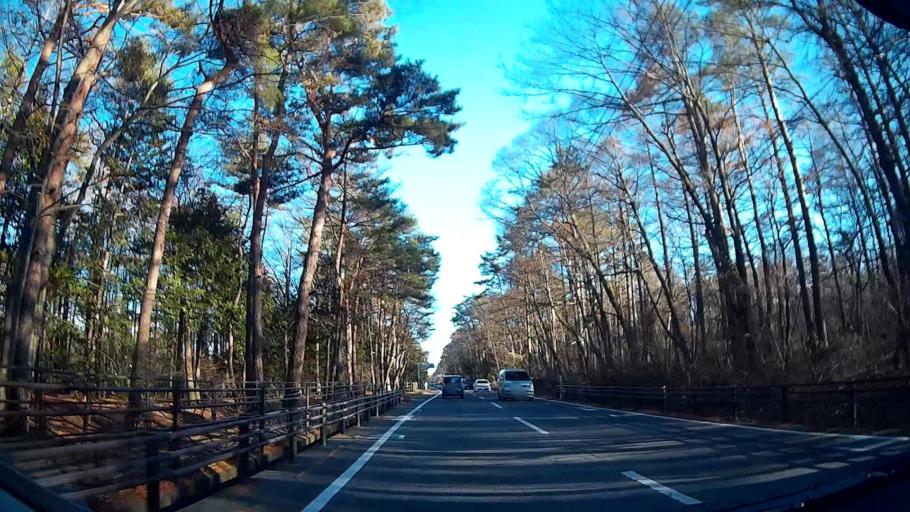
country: JP
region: Yamanashi
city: Fujikawaguchiko
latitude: 35.4488
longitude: 138.8181
